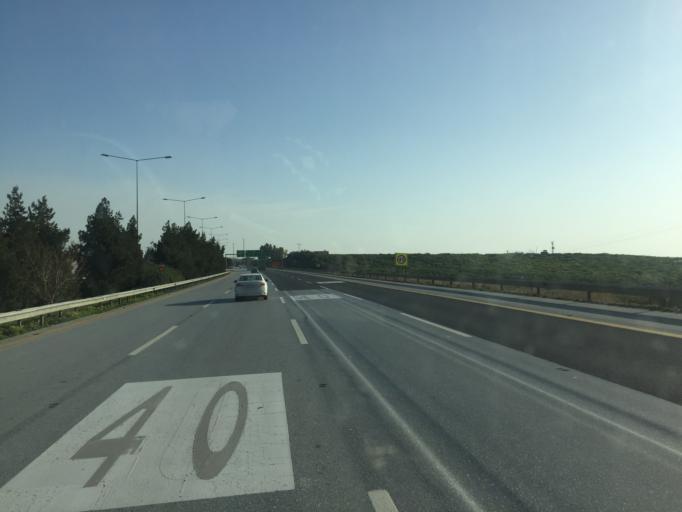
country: TR
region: Mersin
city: Yenice
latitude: 37.0256
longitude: 35.1063
